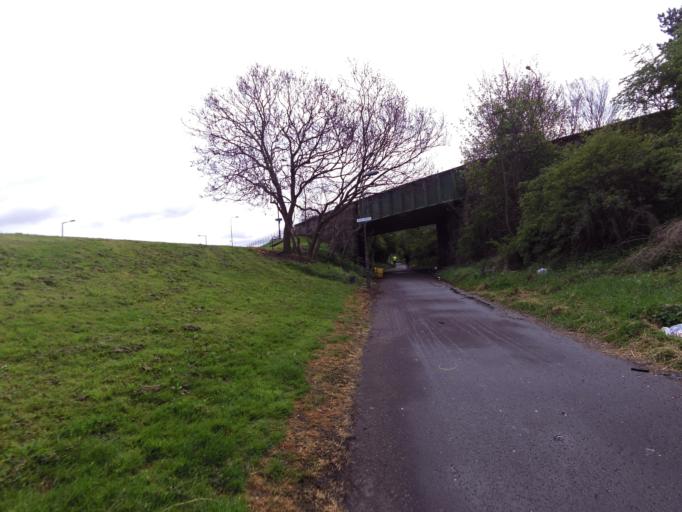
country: GB
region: Scotland
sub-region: Edinburgh
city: Colinton
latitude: 55.9660
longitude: -3.2658
